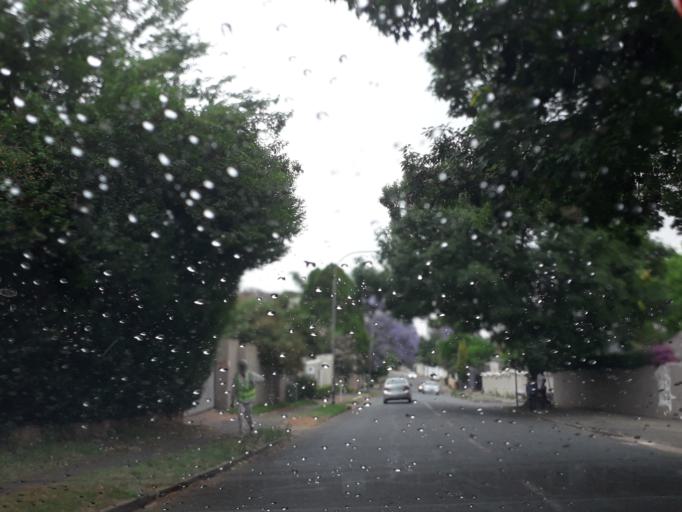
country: ZA
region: Gauteng
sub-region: City of Johannesburg Metropolitan Municipality
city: Johannesburg
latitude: -26.1675
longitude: 28.0763
